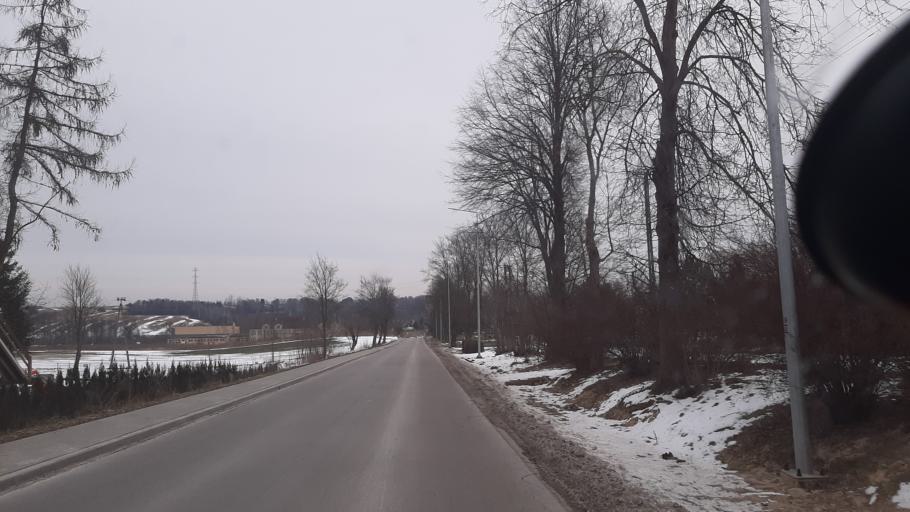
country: PL
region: Lublin Voivodeship
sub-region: Powiat lubelski
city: Jakubowice Murowane
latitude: 51.2967
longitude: 22.6305
